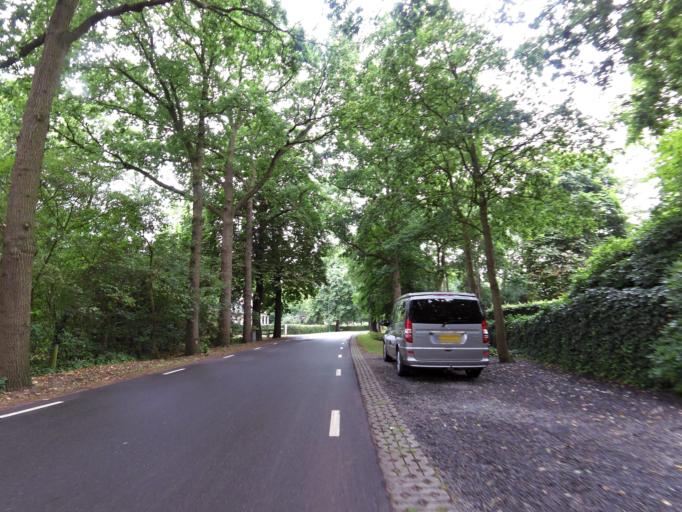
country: NL
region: North Brabant
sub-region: Gemeente Breda
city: Hoge Vucht
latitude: 51.6328
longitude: 4.8080
